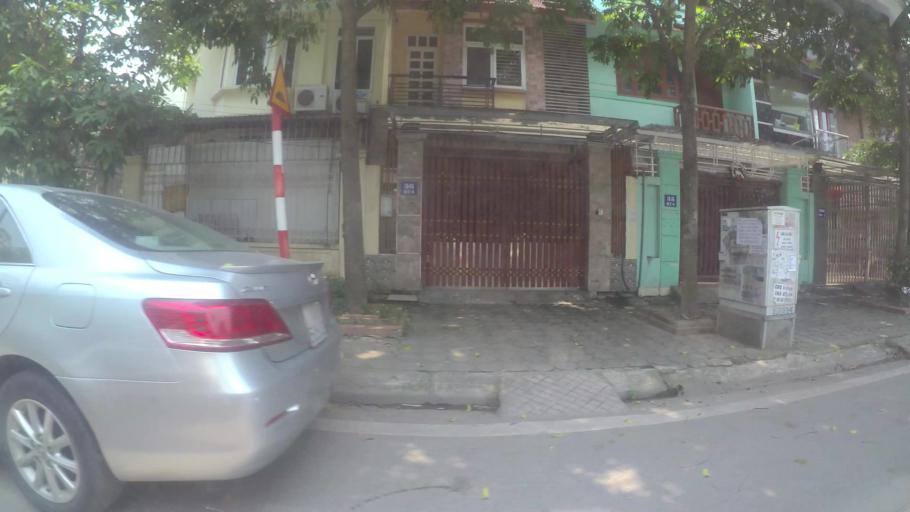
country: VN
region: Ha Noi
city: Ha Dong
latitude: 20.9929
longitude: 105.7782
